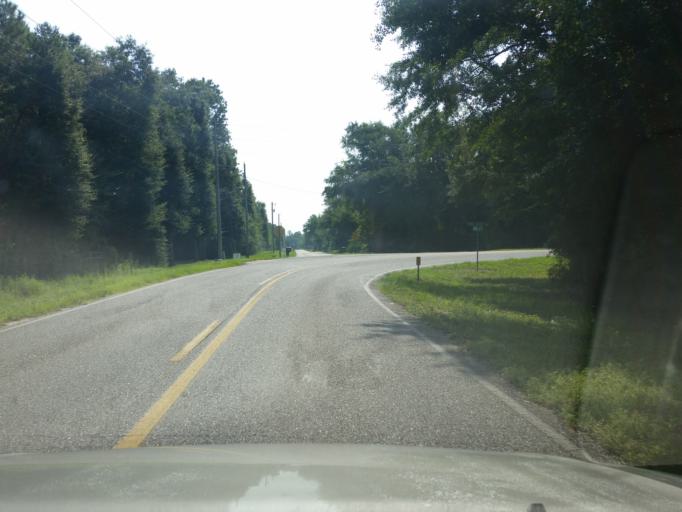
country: US
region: Florida
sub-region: Escambia County
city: Bellview
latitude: 30.5115
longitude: -87.4641
